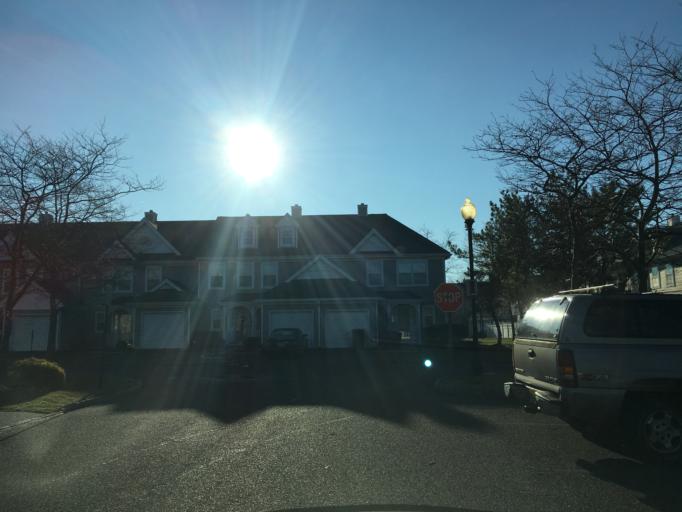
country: US
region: New Jersey
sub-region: Atlantic County
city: Atlantic City
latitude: 39.3743
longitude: -74.4184
